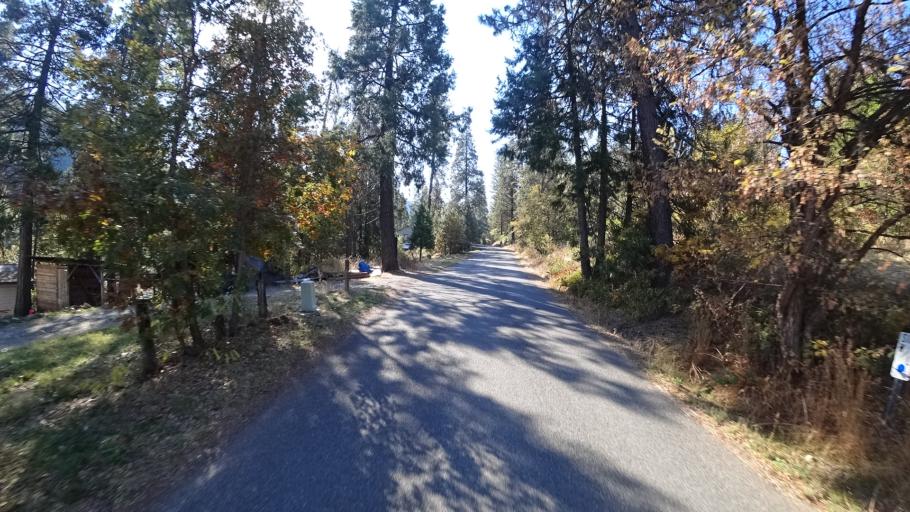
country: US
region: California
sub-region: Siskiyou County
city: Yreka
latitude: 41.7396
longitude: -123.0040
